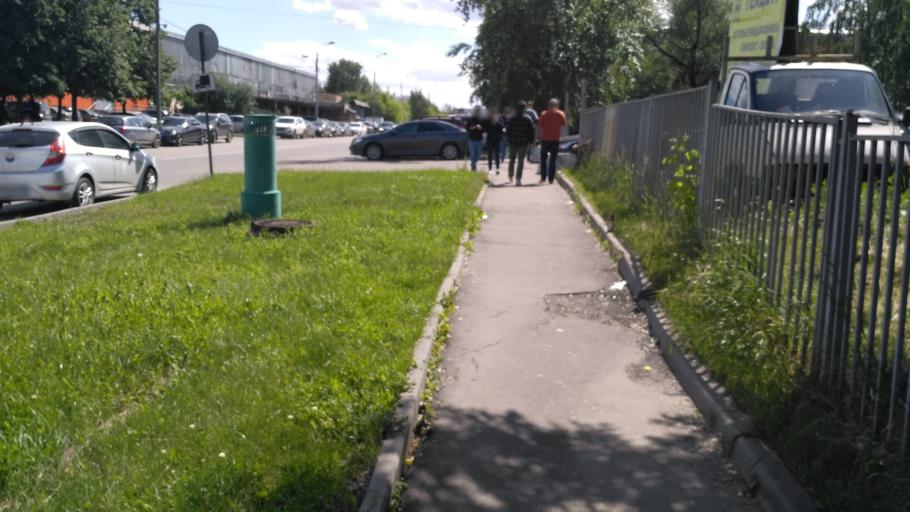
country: RU
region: Moscow
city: Kozeyevo
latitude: 55.8887
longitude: 37.6353
